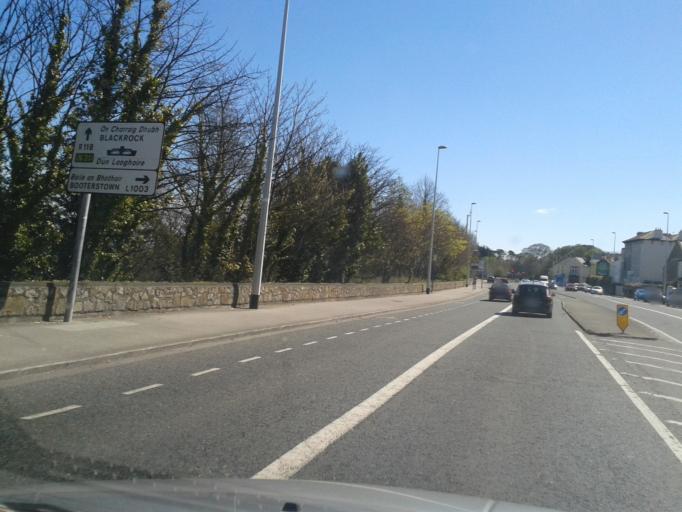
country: IE
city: Booterstown
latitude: 53.3101
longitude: -6.1987
